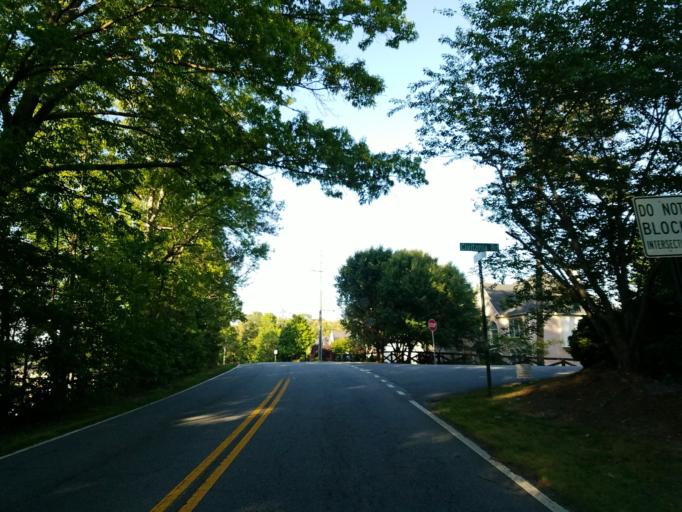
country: US
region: Georgia
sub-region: Cobb County
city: Mableton
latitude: 33.8319
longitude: -84.5397
